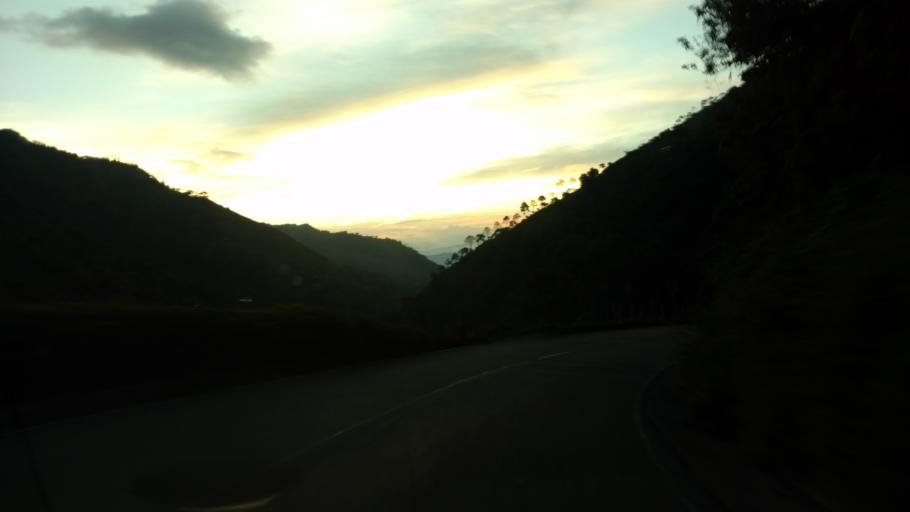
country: CO
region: Caldas
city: Aranzazu
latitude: 5.2555
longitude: -75.5029
